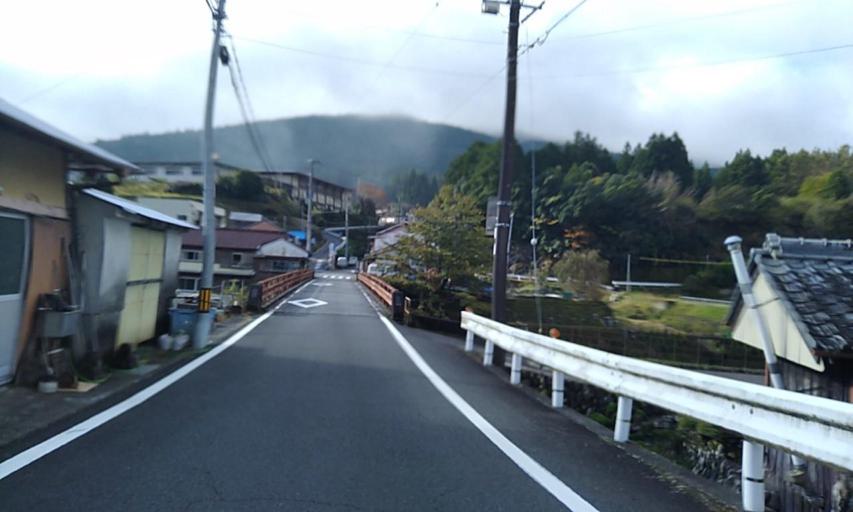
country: JP
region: Wakayama
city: Shingu
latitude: 33.9234
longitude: 135.9831
